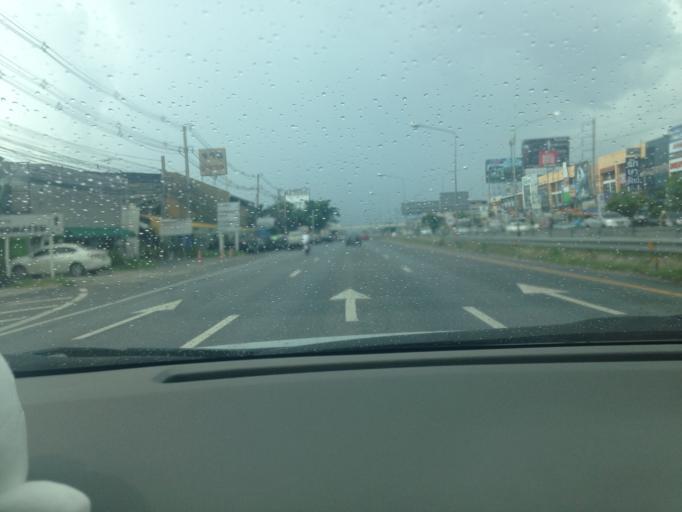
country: TH
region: Chon Buri
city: Chon Buri
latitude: 13.2950
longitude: 100.9447
